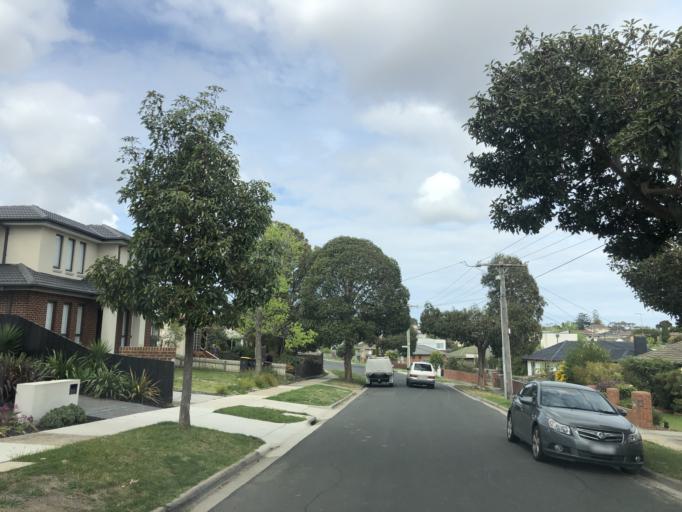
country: AU
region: Victoria
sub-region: Monash
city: Chadstone
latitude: -37.8777
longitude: 145.0968
